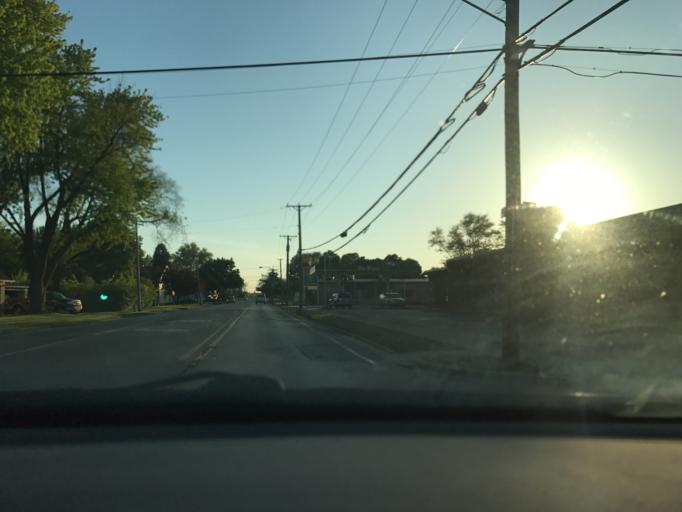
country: US
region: Illinois
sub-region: Kane County
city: Elgin
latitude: 42.0364
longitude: -88.3056
